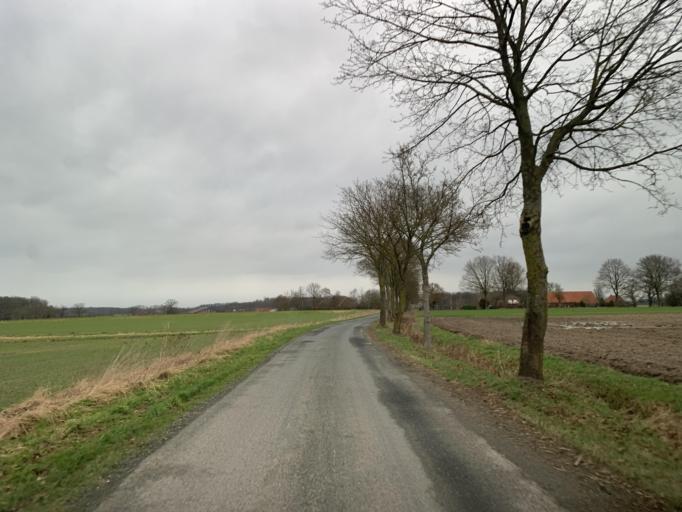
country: DE
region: North Rhine-Westphalia
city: Ludinghausen
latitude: 51.8068
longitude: 7.4679
